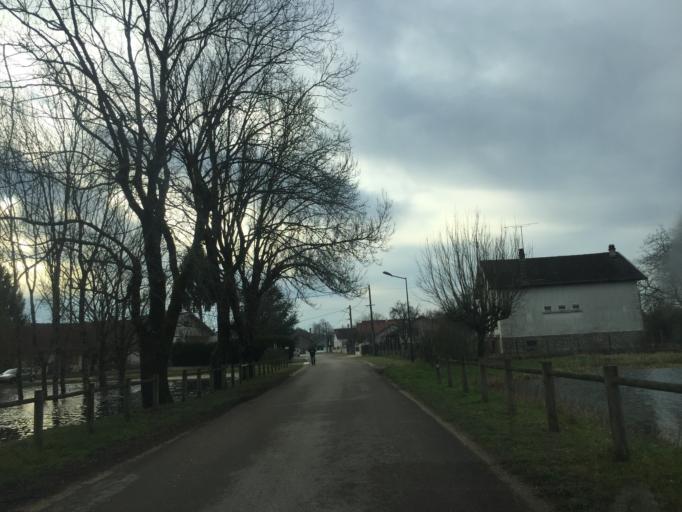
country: FR
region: Franche-Comte
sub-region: Departement du Jura
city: Tavaux
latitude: 47.0170
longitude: 5.4204
